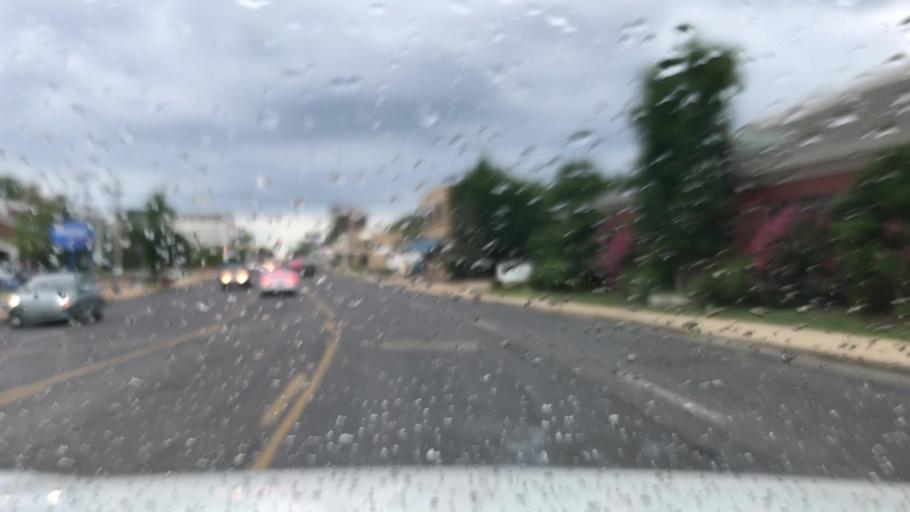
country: US
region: Missouri
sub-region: Saint Louis County
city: Maplewood
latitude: 38.5937
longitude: -90.2992
